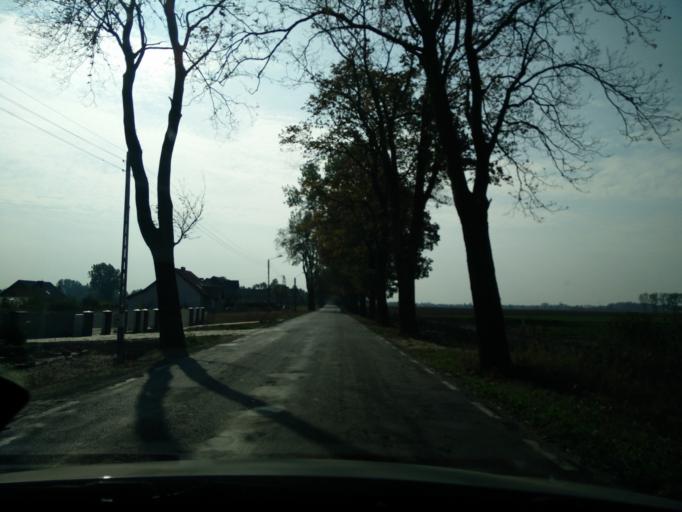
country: PL
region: Greater Poland Voivodeship
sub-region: Powiat sredzki
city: Sroda Wielkopolska
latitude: 52.2502
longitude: 17.2961
